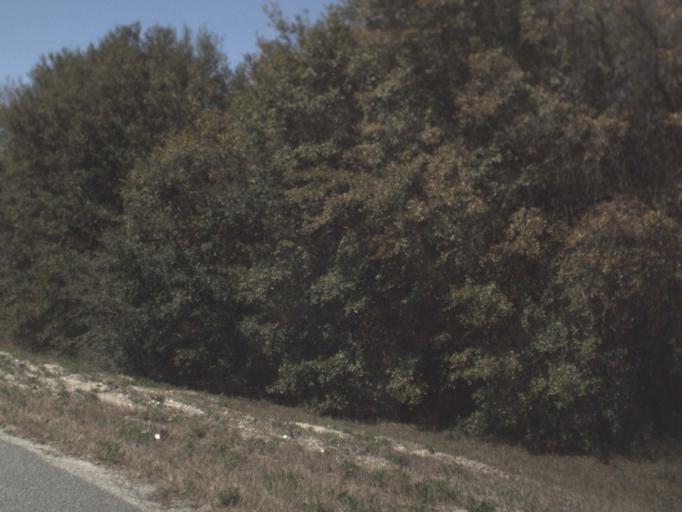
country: US
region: Florida
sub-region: Franklin County
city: Carrabelle
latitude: 29.9332
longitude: -84.4436
